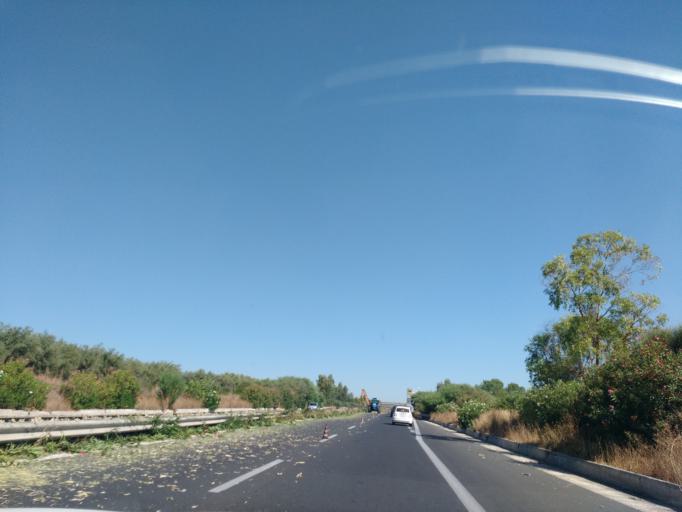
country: IT
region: Sicily
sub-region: Provincia di Siracusa
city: Priolo Gargallo
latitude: 37.1686
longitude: 15.1599
